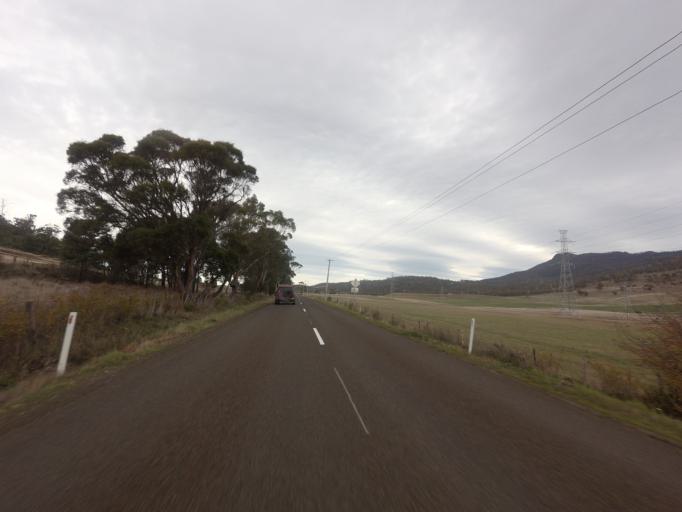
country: AU
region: Tasmania
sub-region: Brighton
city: Bridgewater
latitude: -42.6638
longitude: 147.1306
